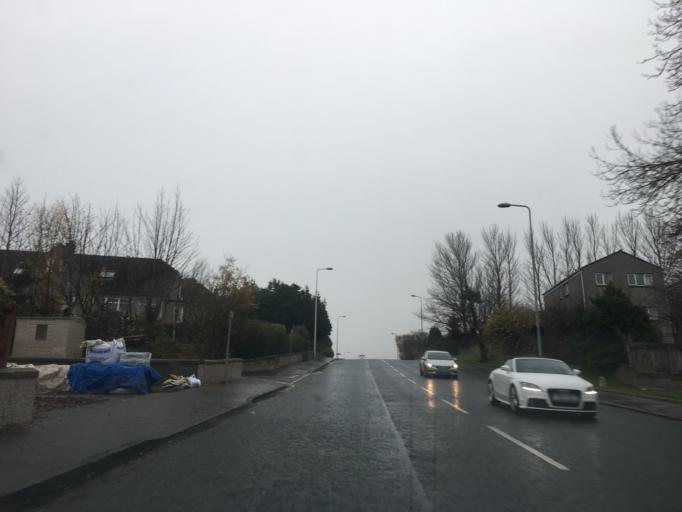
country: GB
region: Scotland
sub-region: Edinburgh
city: Currie
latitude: 55.9567
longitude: -3.2991
